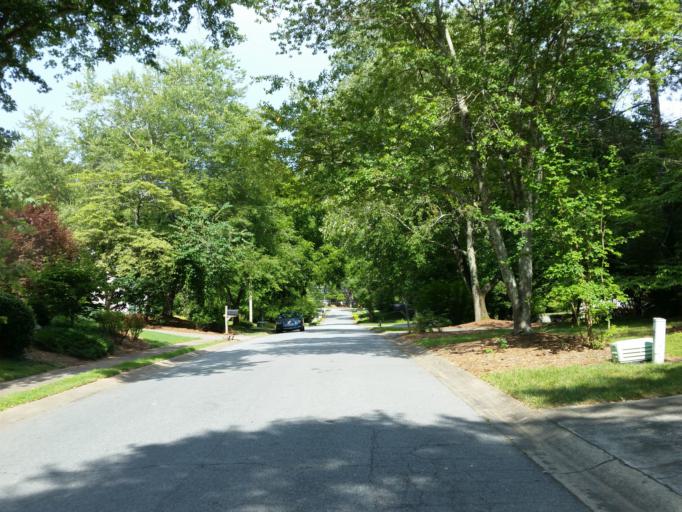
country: US
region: Georgia
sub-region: Cobb County
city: Marietta
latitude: 34.0014
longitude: -84.4717
